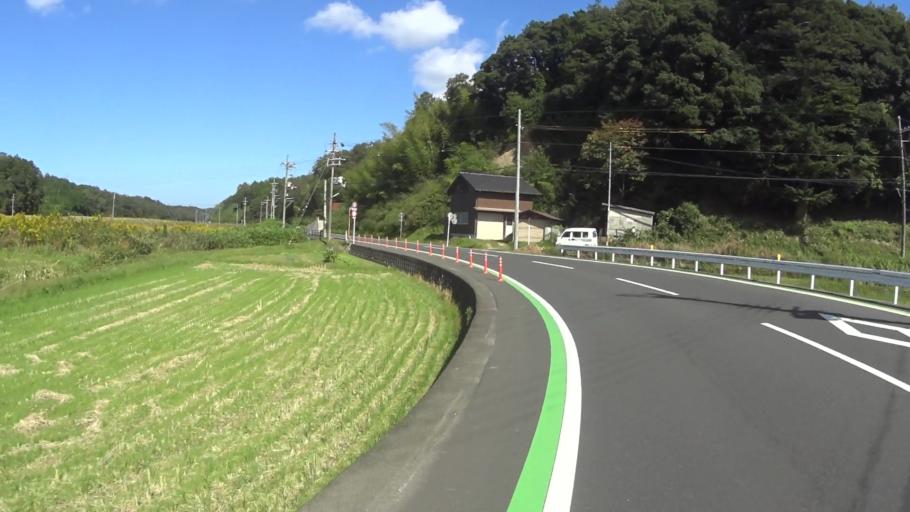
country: JP
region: Kyoto
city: Miyazu
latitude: 35.6408
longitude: 135.0726
